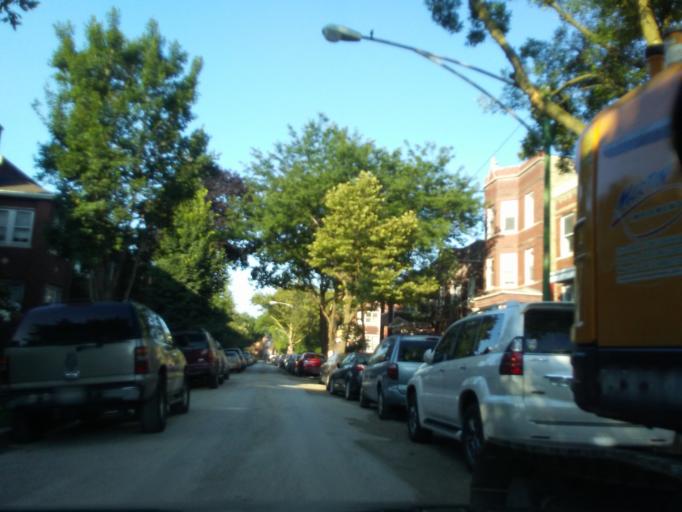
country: US
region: Illinois
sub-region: Cook County
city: Lincolnwood
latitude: 41.9369
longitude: -87.7230
